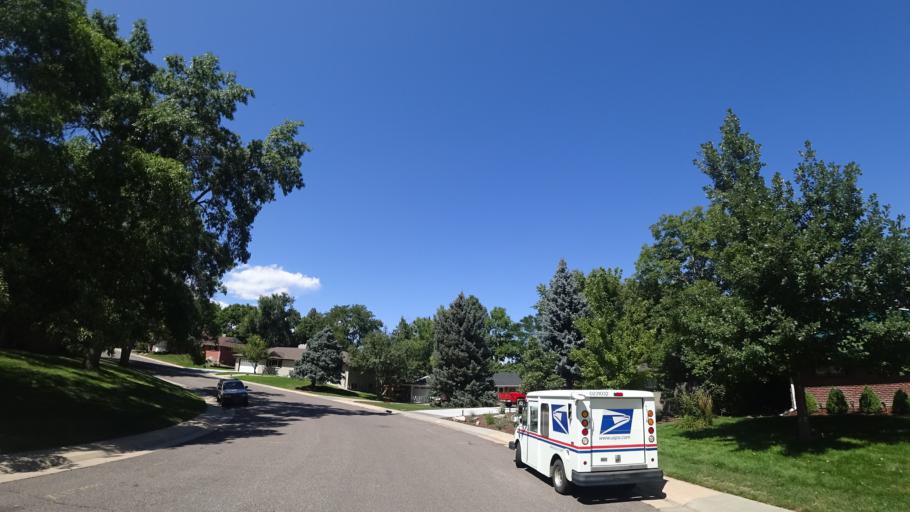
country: US
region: Colorado
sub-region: Arapahoe County
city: Greenwood Village
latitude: 39.6085
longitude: -104.9772
